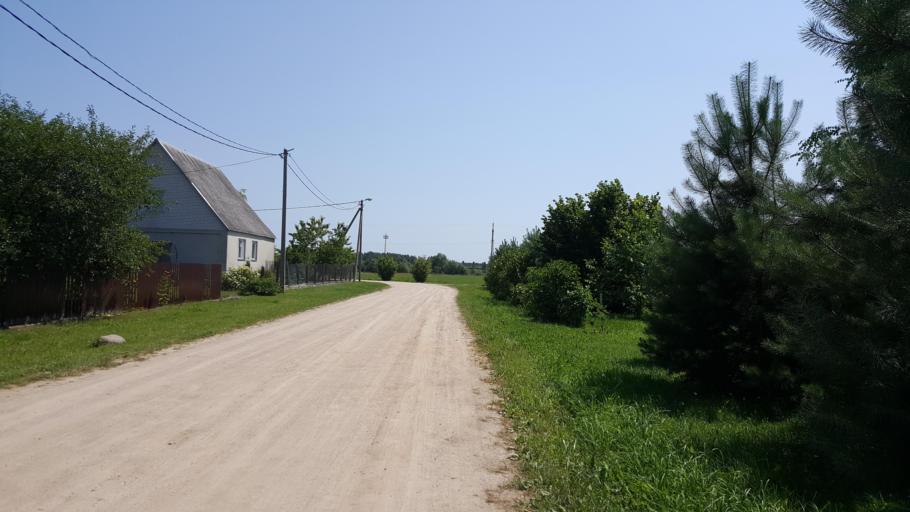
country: BY
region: Brest
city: Zhabinka
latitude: 52.1882
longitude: 24.0035
